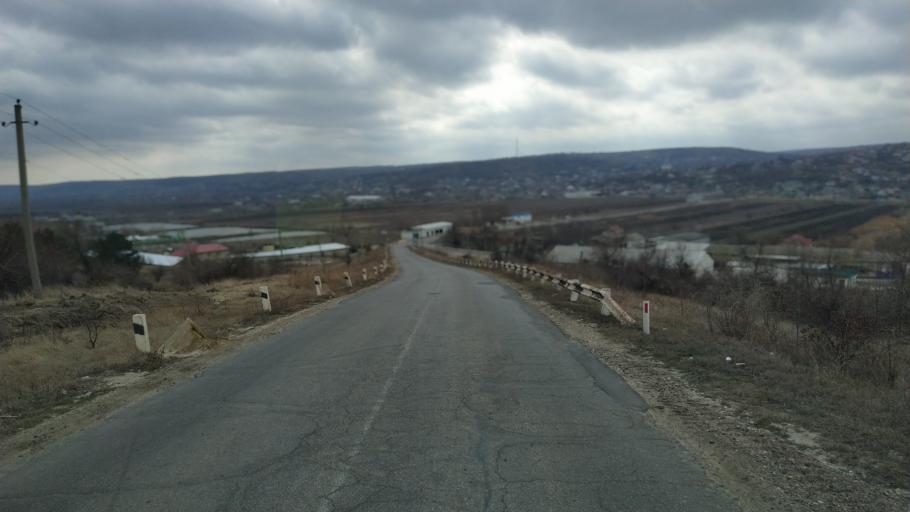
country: MD
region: Laloveni
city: Ialoveni
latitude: 46.8817
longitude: 28.7669
